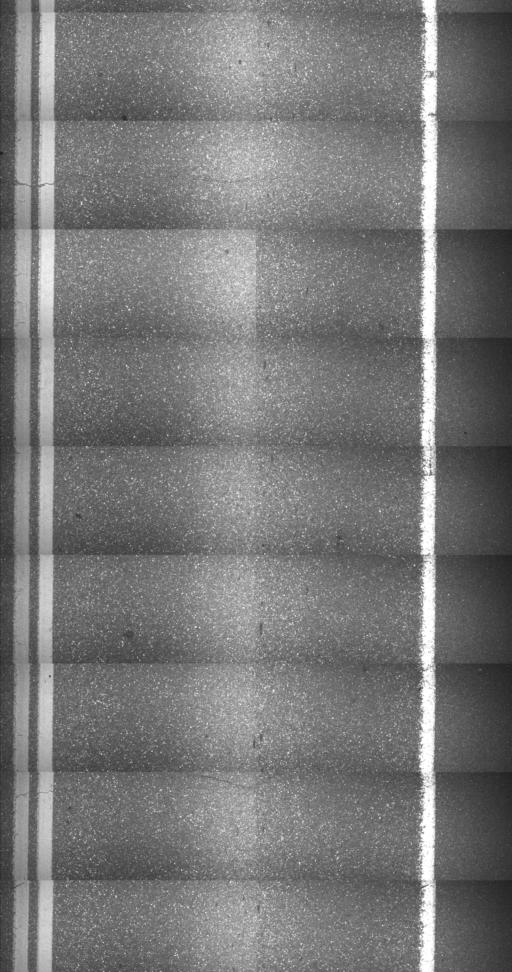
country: US
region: Vermont
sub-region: Washington County
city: Montpelier
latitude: 44.2585
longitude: -72.5929
